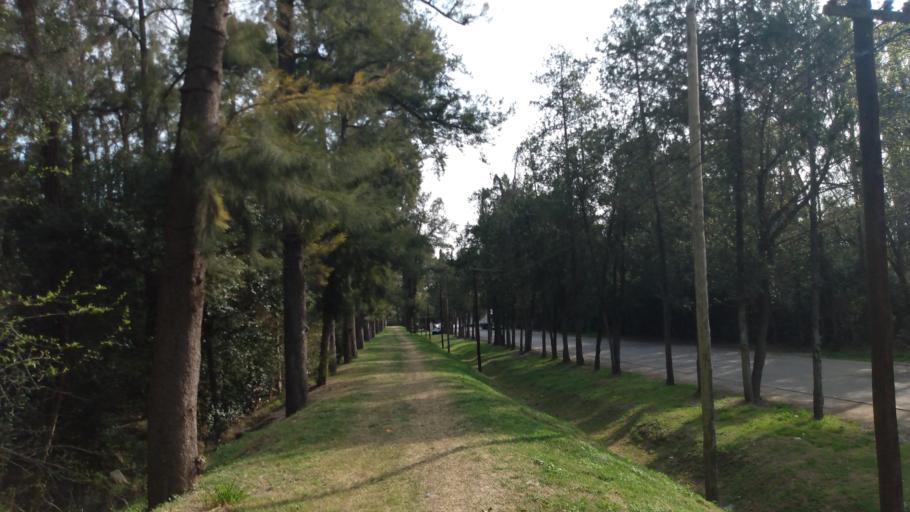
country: AR
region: Buenos Aires
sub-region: Partido de Lujan
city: Lujan
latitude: -34.5892
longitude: -59.1820
